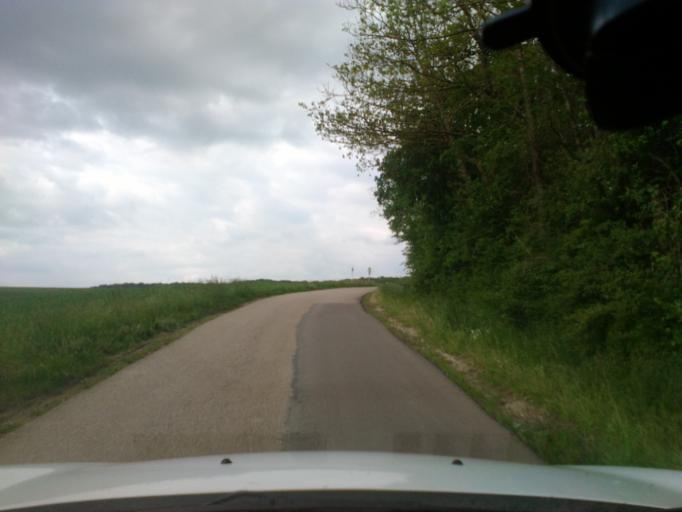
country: FR
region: Lorraine
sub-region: Departement des Vosges
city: Mirecourt
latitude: 48.3435
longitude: 6.1038
